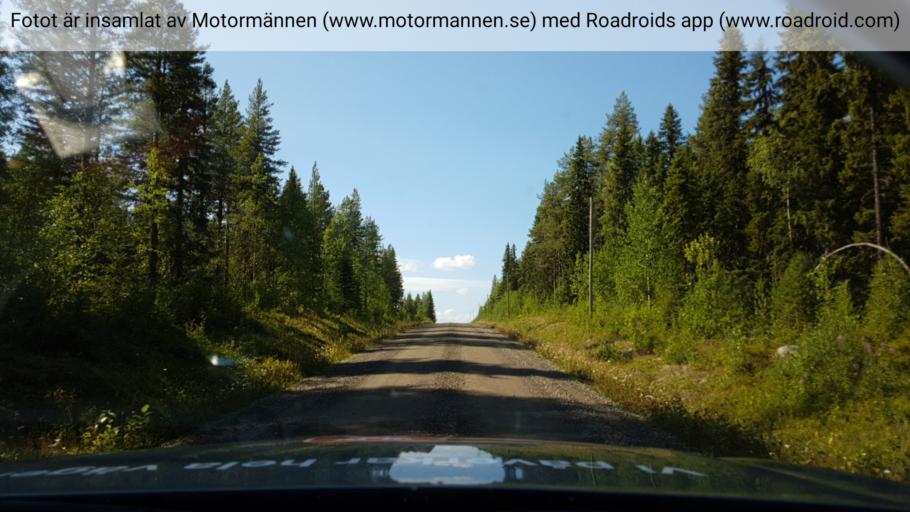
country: SE
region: Vaesterbotten
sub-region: Dorotea Kommun
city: Dorotea
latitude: 64.0930
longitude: 16.5084
